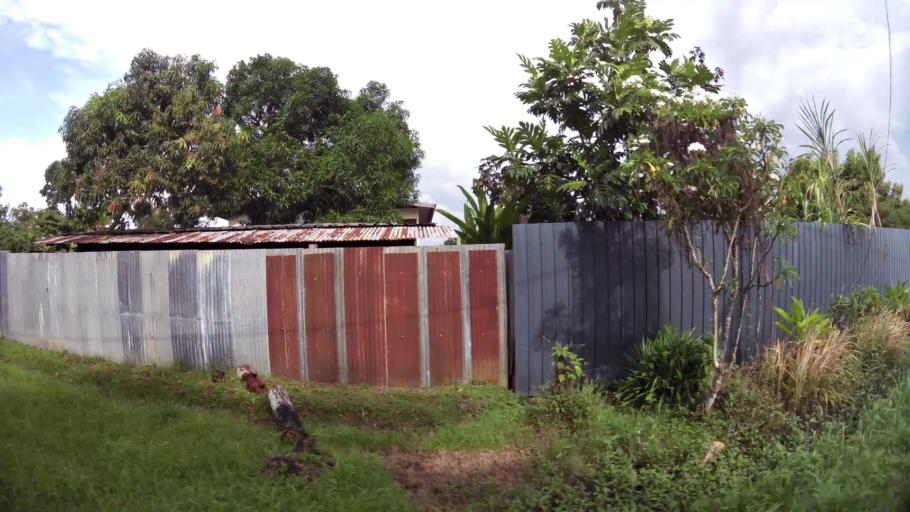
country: SR
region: Paramaribo
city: Paramaribo
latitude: 5.8520
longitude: -55.1549
